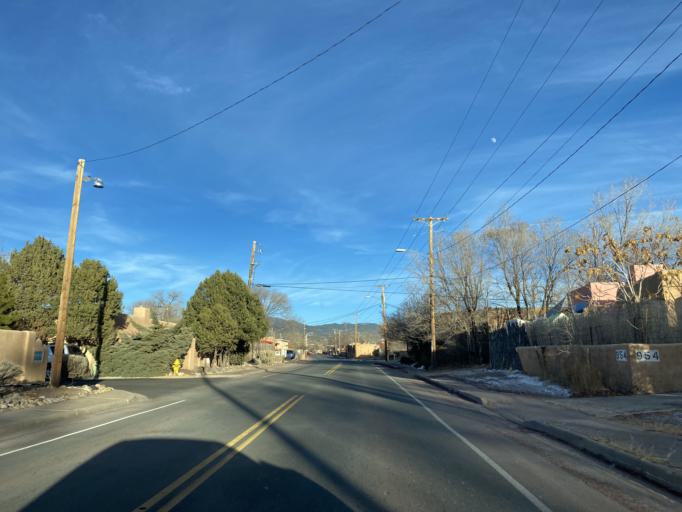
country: US
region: New Mexico
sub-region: Santa Fe County
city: Santa Fe
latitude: 35.6833
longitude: -105.9580
